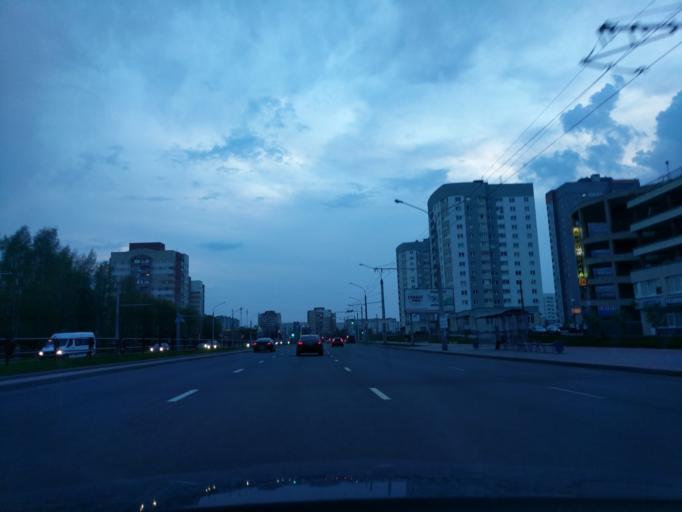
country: BY
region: Minsk
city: Novoye Medvezhino
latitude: 53.8719
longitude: 27.4814
